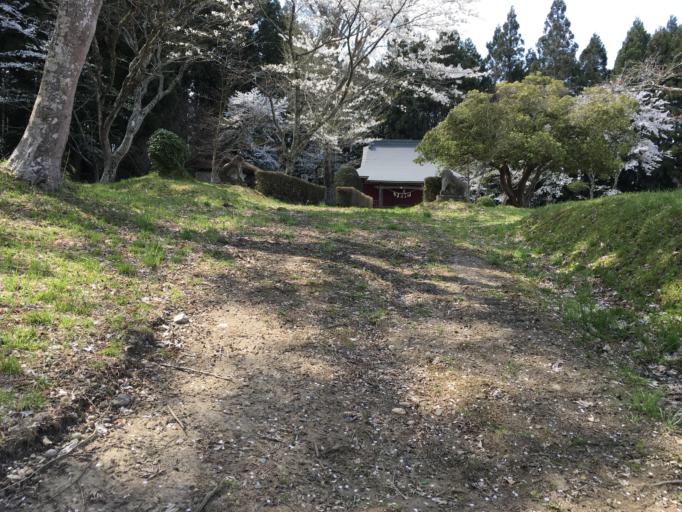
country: JP
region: Iwate
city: Ichinoseki
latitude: 38.8485
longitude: 141.1591
